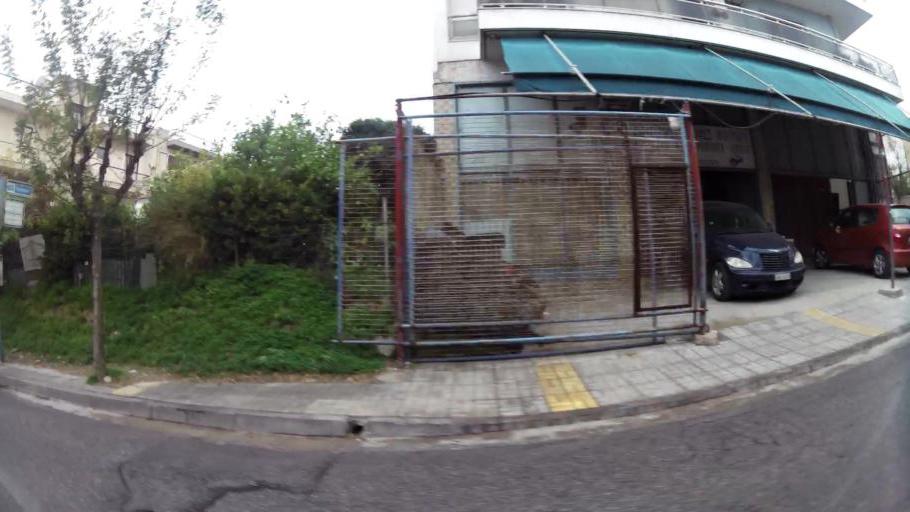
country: GR
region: Attica
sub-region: Nomarchia Athinas
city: Ilion
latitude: 38.0245
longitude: 23.7061
